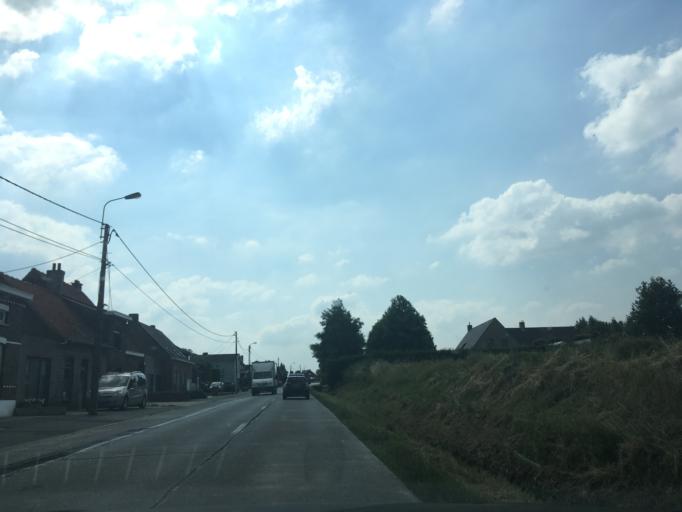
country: BE
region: Flanders
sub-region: Provincie West-Vlaanderen
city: Staden
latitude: 50.9722
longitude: 3.0000
